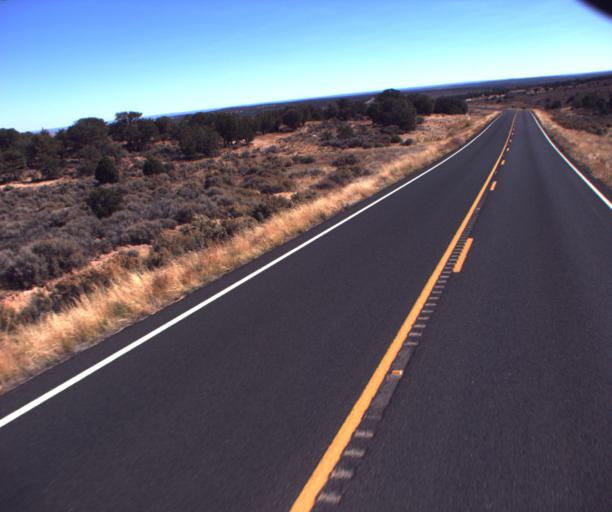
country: US
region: Arizona
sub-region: Apache County
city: Ganado
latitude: 35.7640
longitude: -109.7870
